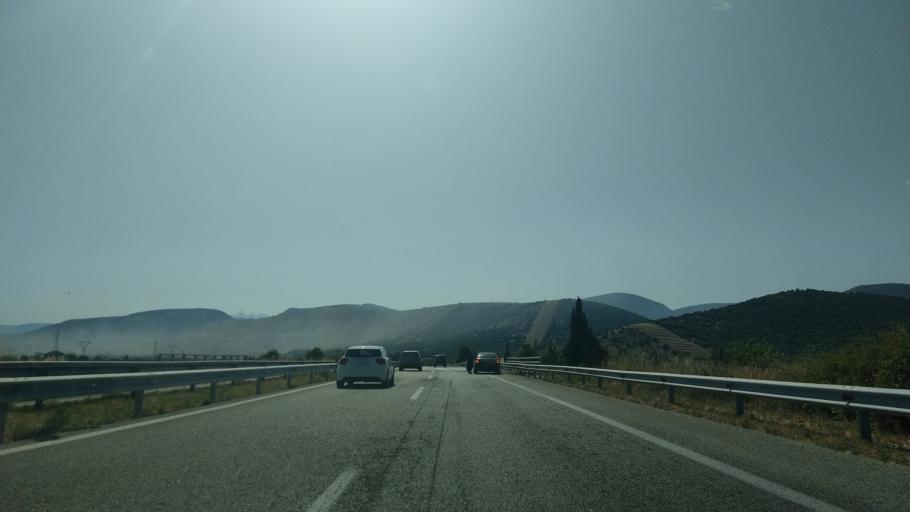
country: GR
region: East Macedonia and Thrace
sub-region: Nomos Kavalas
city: Nea Karvali
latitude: 40.9701
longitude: 24.5038
